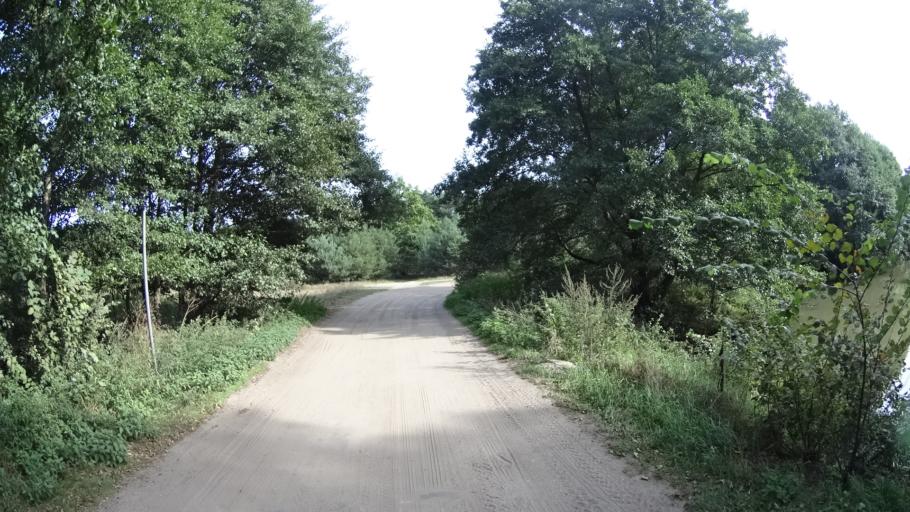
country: PL
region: Masovian Voivodeship
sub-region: Powiat legionowski
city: Serock
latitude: 52.4998
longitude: 21.0880
